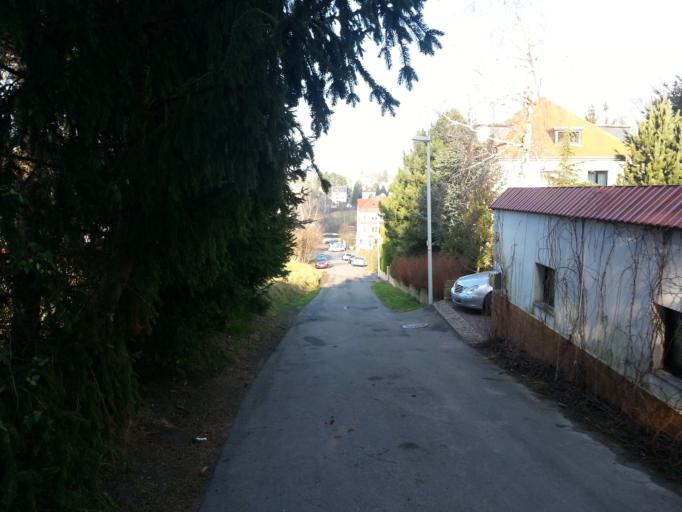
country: DE
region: Saxony
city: Bannewitz
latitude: 51.0116
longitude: 13.7300
